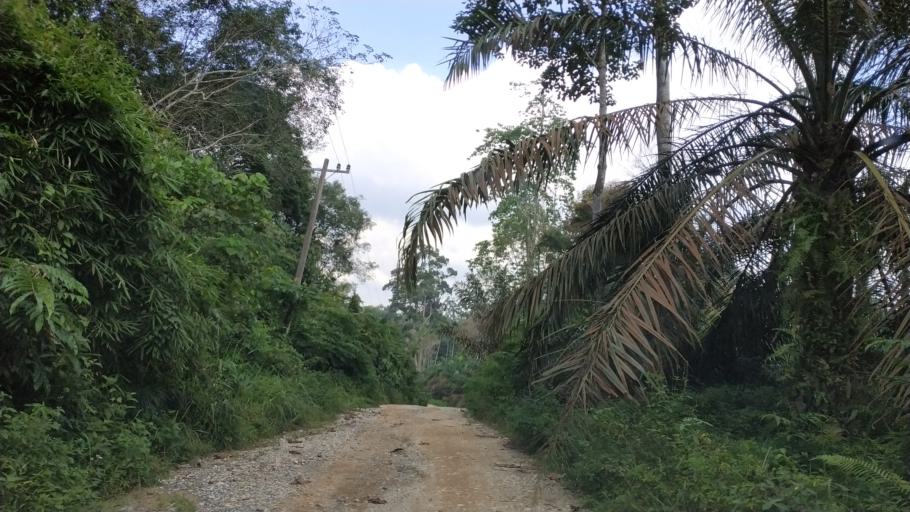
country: ID
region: Riau
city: Pangkalan Kasai
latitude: -0.7263
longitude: 102.4750
